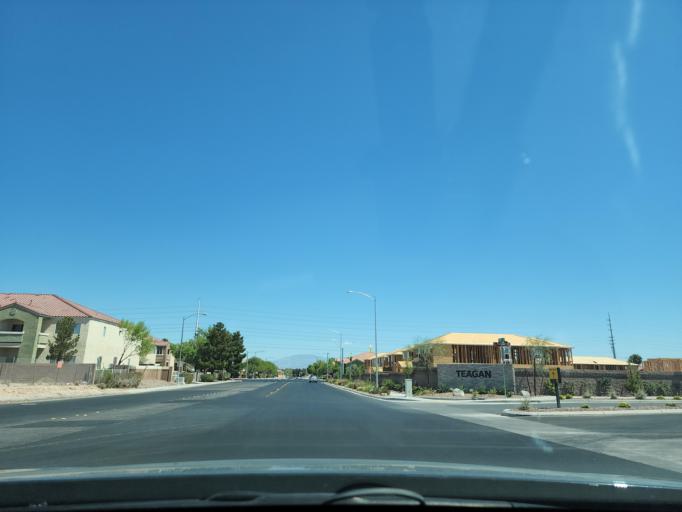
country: US
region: Nevada
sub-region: Clark County
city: Spring Valley
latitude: 36.0838
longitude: -115.2518
